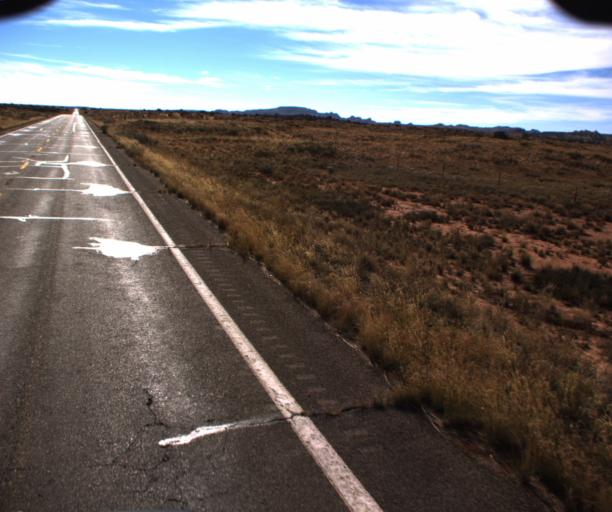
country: US
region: Arizona
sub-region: Coconino County
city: Kaibito
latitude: 36.6082
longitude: -111.1814
